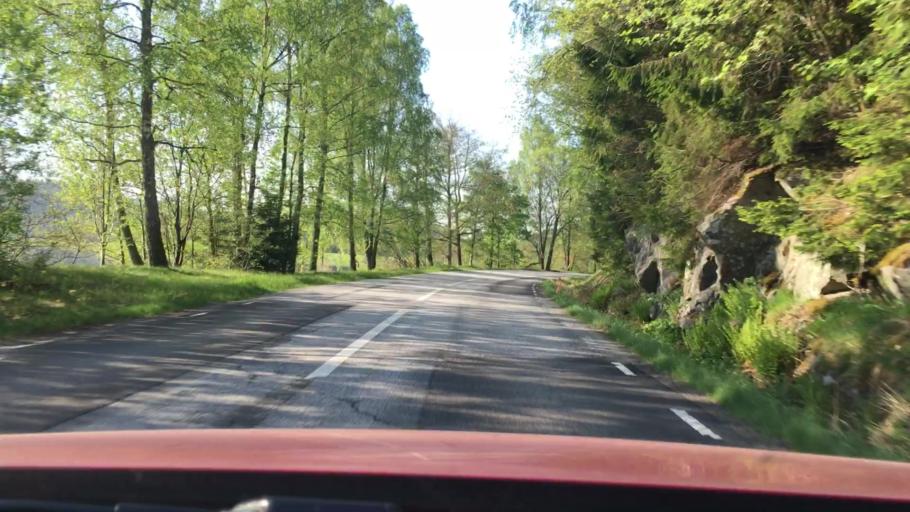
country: SE
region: Vaestra Goetaland
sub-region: Munkedals Kommun
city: Munkedal
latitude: 58.6256
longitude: 11.5600
